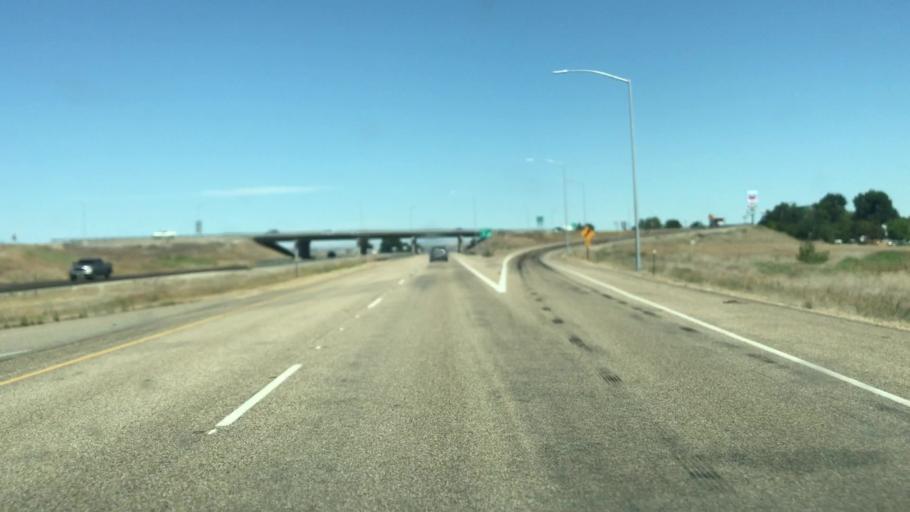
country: US
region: Idaho
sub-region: Payette County
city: Fruitland
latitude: 43.9696
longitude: -116.9117
